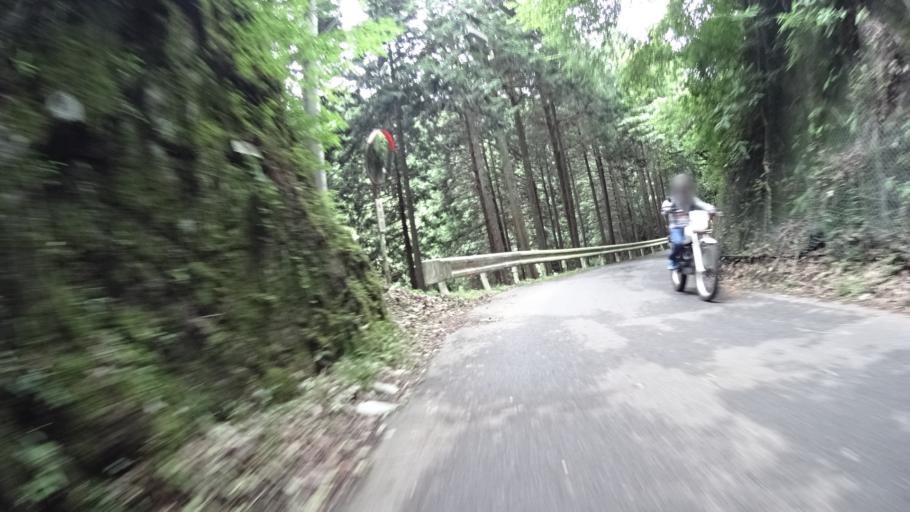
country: JP
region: Kanagawa
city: Hadano
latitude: 35.4988
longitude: 139.2266
